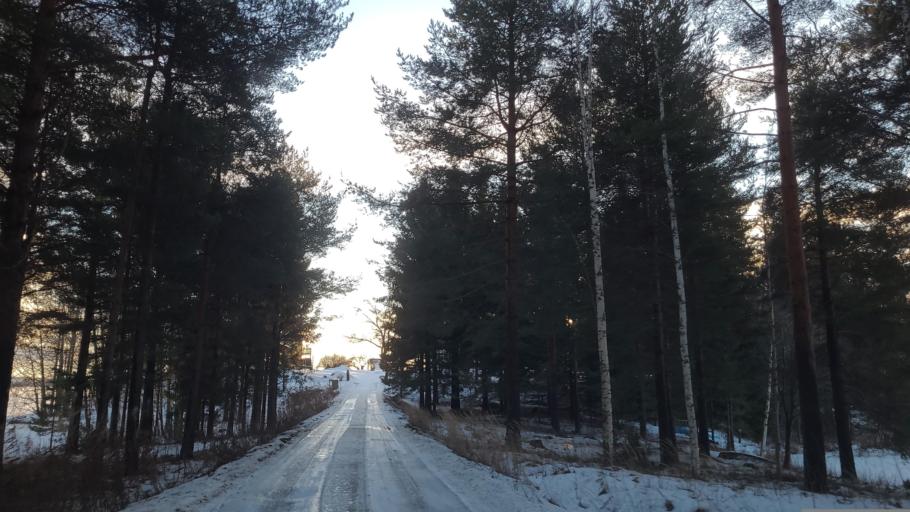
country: SE
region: Gaevleborg
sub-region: Bollnas Kommun
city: Bollnas
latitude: 61.3505
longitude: 16.4093
